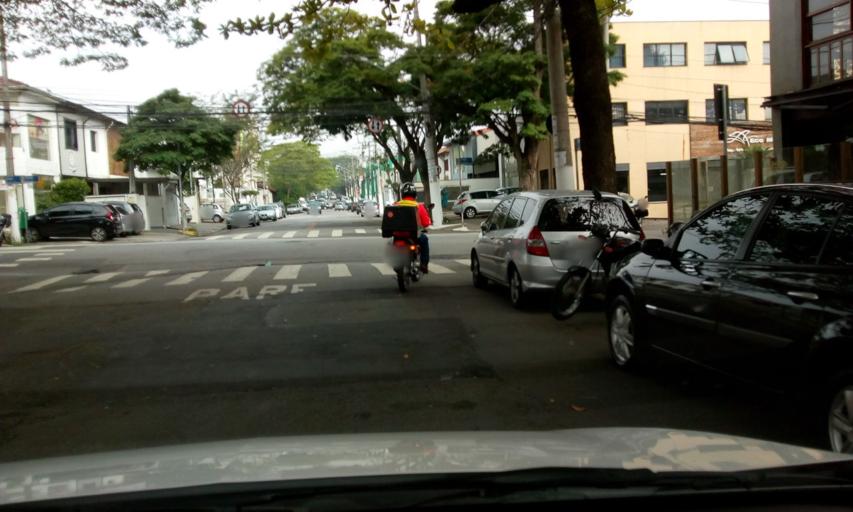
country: BR
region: Sao Paulo
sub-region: Sao Paulo
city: Sao Paulo
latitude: -23.6132
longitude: -46.6686
